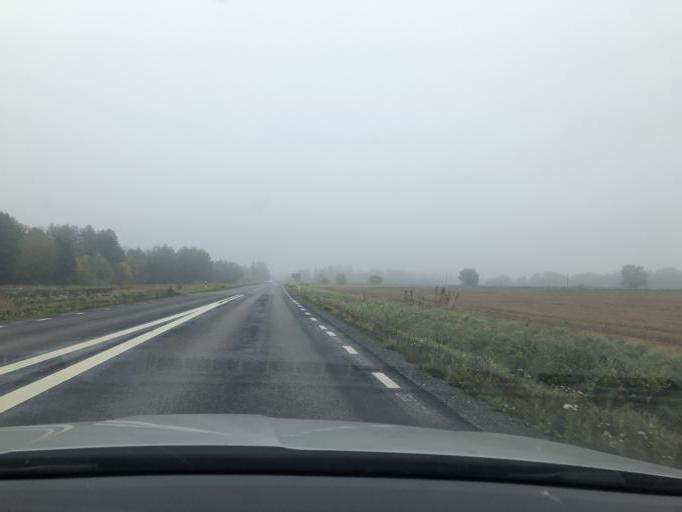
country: SE
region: Uppsala
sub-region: Tierps Kommun
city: Tierp
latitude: 60.3367
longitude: 17.5054
